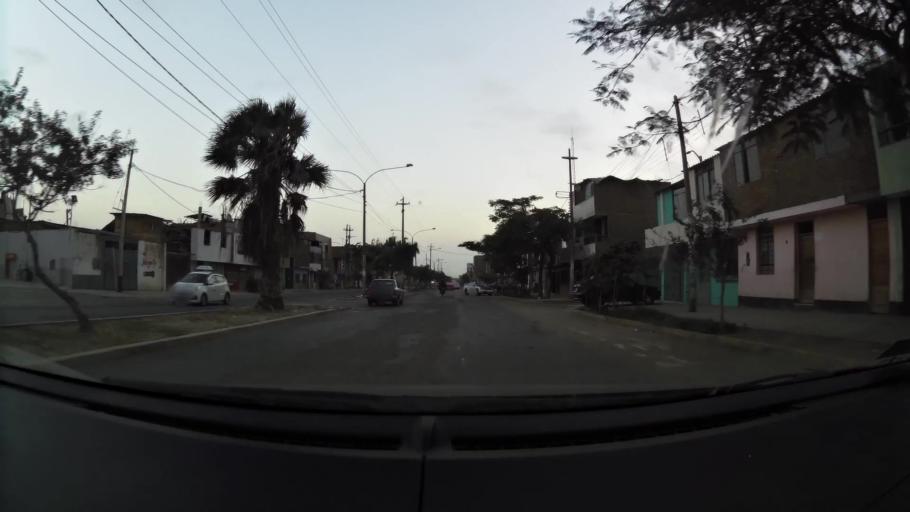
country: PE
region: La Libertad
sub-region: Provincia de Trujillo
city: El Porvenir
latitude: -8.0867
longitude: -79.0150
